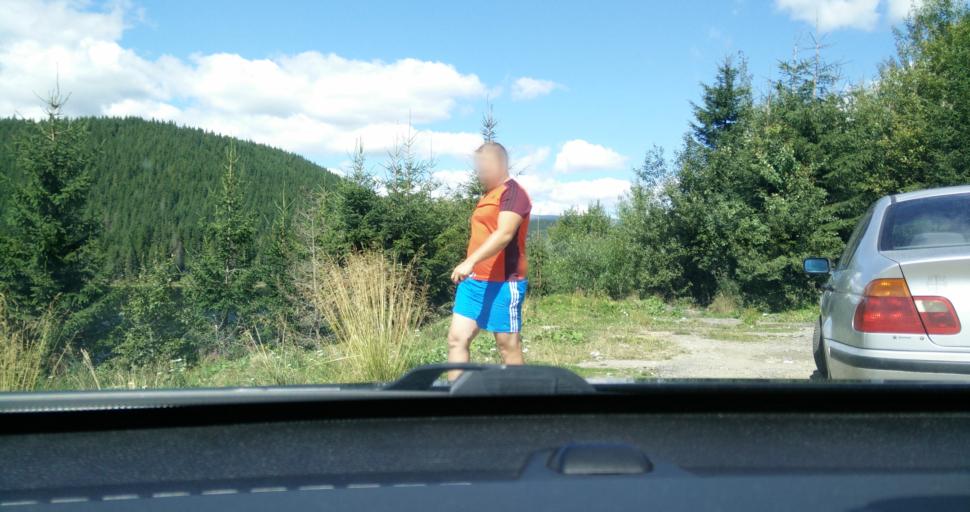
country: RO
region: Alba
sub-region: Comuna Sugag
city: Sugag
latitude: 45.5489
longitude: 23.6312
